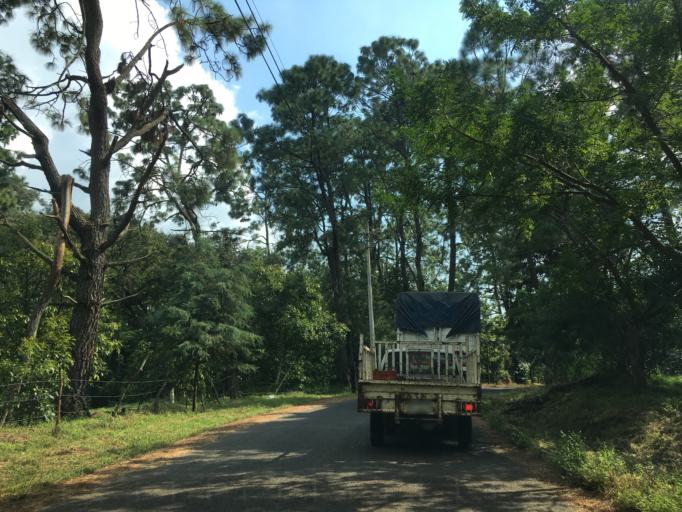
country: MX
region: Michoacan
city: Tingambato
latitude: 19.4548
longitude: -101.8662
